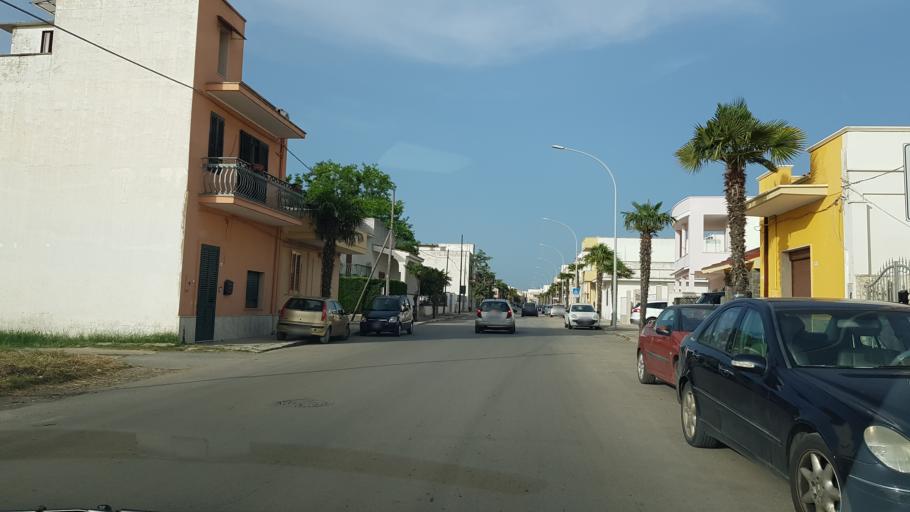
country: IT
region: Apulia
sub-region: Provincia di Brindisi
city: San Donaci
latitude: 40.4449
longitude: 17.9152
